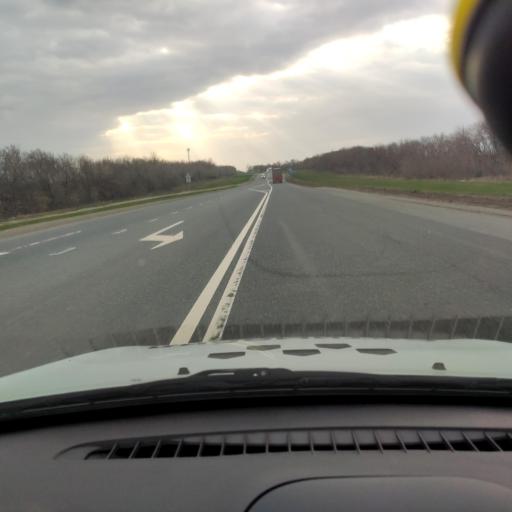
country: RU
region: Samara
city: Mezhdurechensk
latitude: 53.2538
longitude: 49.1452
